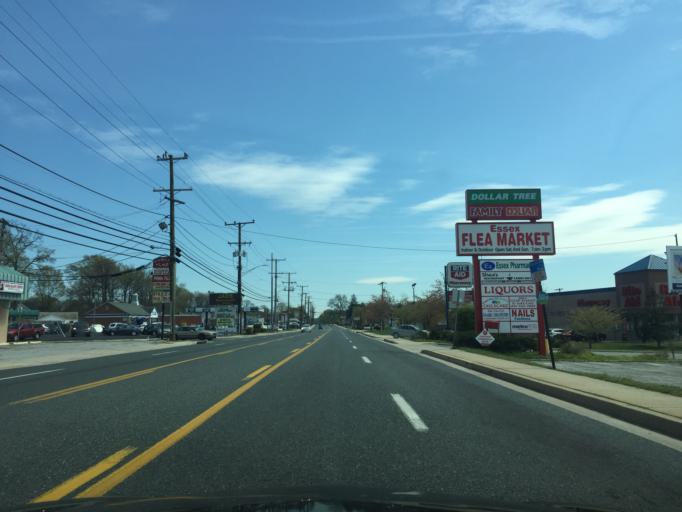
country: US
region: Maryland
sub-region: Baltimore County
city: Middle River
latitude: 39.3103
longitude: -76.4464
